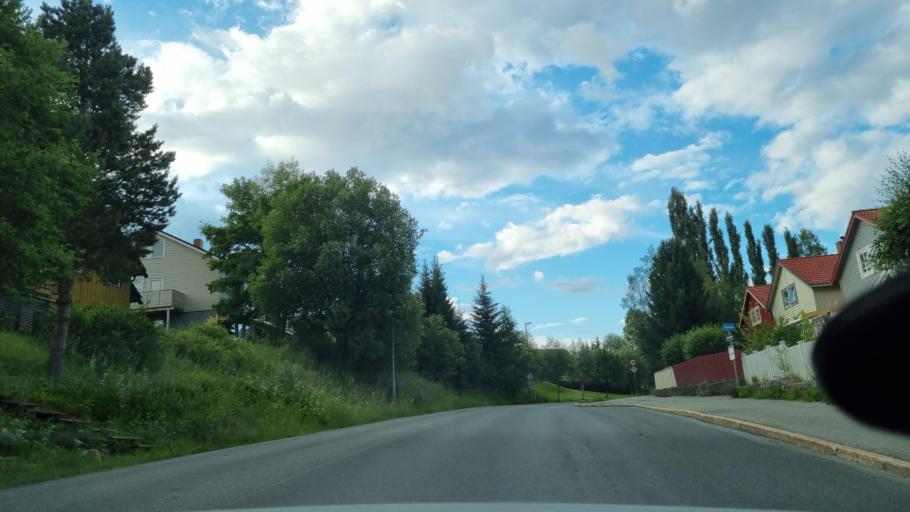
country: NO
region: Sor-Trondelag
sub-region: Trondheim
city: Trondheim
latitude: 63.3840
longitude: 10.3272
